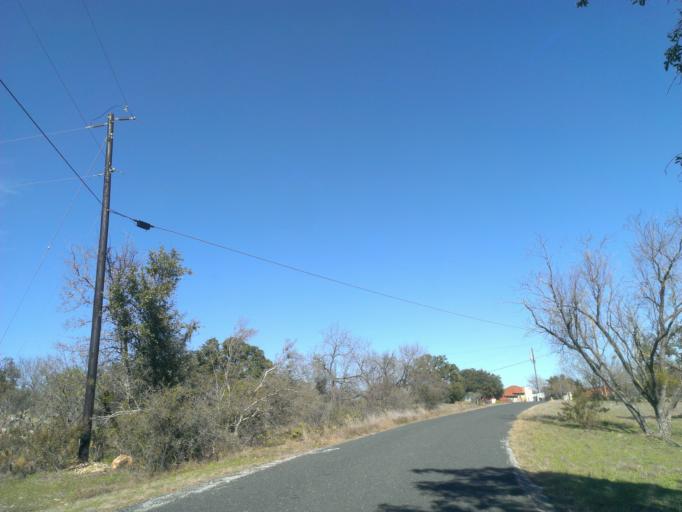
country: US
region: Texas
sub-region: Travis County
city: Briarcliff
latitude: 30.4338
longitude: -98.0656
